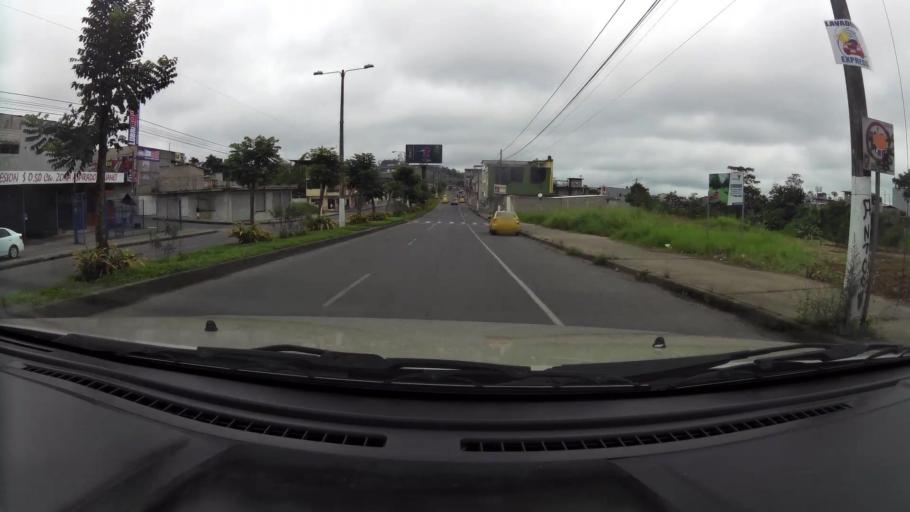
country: EC
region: Santo Domingo de los Tsachilas
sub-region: Canton Santo Domingo de los Colorados
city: Santo Domingo de los Colorados
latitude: -0.2392
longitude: -79.1803
